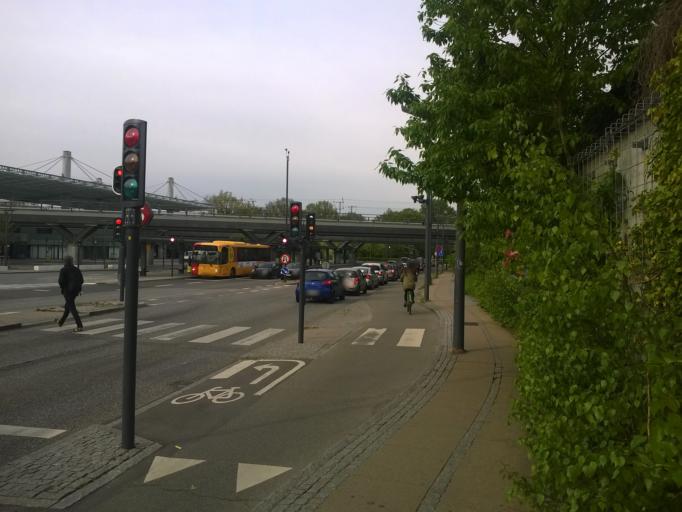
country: DK
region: Capital Region
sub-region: Kobenhavn
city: Vanlose
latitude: 55.6867
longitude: 12.4990
